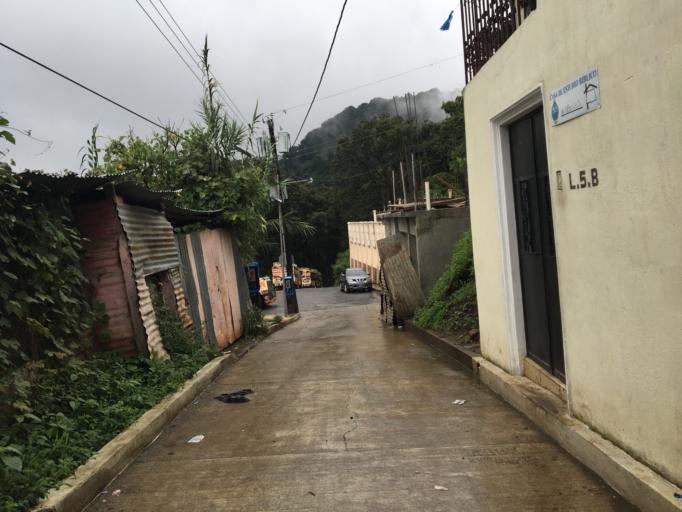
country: GT
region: Guatemala
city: Santa Catarina Pinula
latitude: 14.5434
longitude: -90.4998
